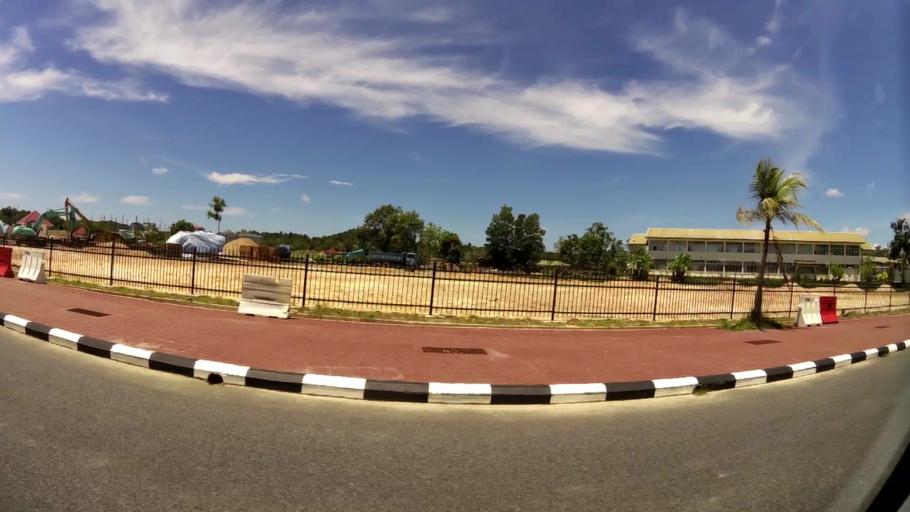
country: BN
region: Brunei and Muara
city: Bandar Seri Begawan
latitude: 4.9274
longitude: 114.9420
